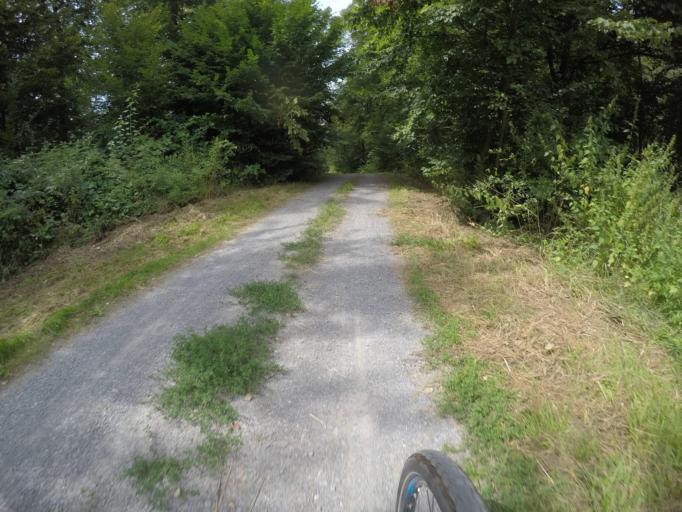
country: DE
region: Baden-Wuerttemberg
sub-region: Karlsruhe Region
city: Hambrucken
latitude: 49.2072
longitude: 8.5440
